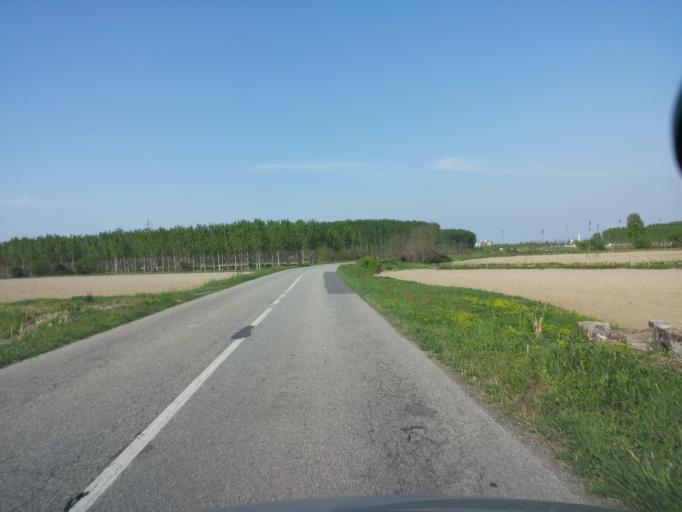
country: IT
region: Lombardy
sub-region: Provincia di Pavia
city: Albonese
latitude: 45.3005
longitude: 8.7169
